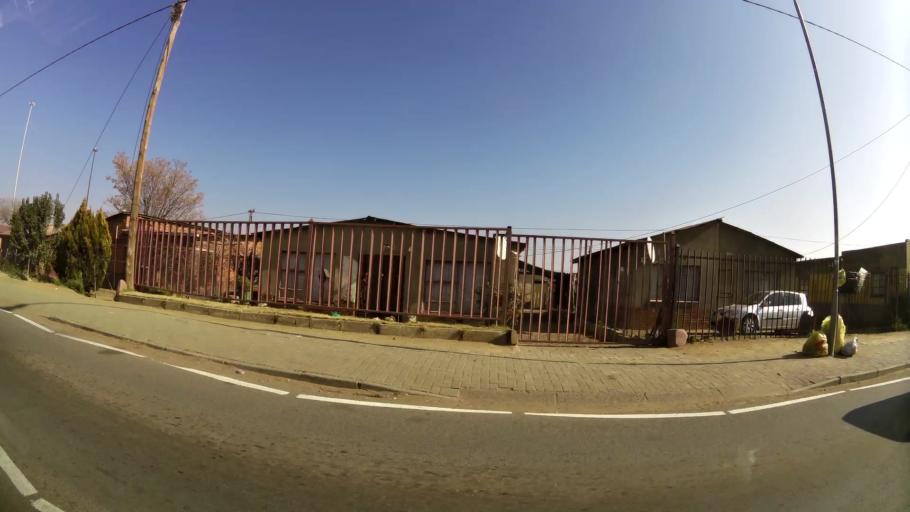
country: ZA
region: Orange Free State
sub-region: Mangaung Metropolitan Municipality
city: Bloemfontein
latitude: -29.1639
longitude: 26.2374
